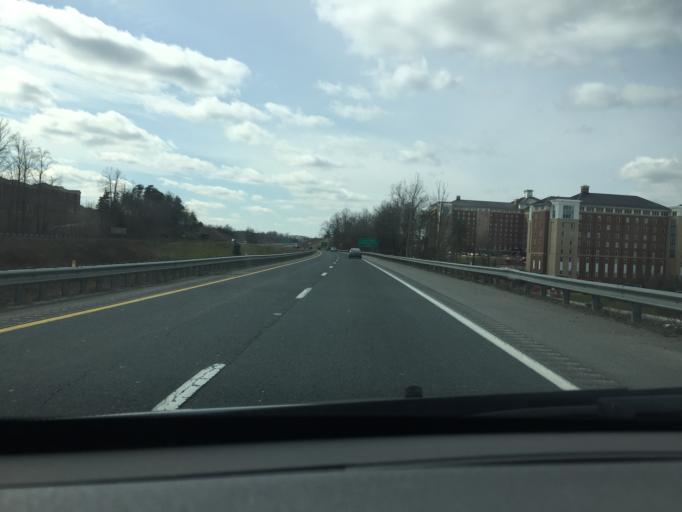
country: US
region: Virginia
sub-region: City of Lynchburg
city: West Lynchburg
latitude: 37.3489
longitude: -79.1789
